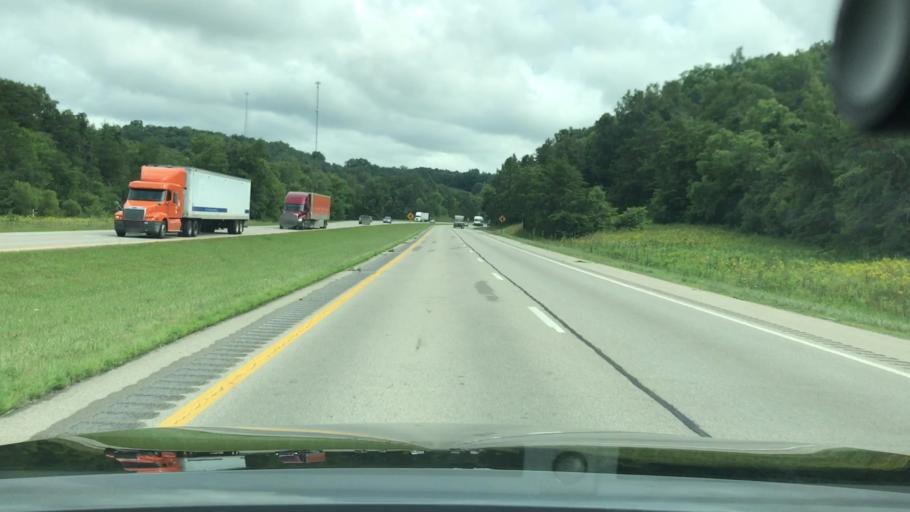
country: US
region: Ohio
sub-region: Jackson County
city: Oak Hill
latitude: 38.9377
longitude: -82.4705
